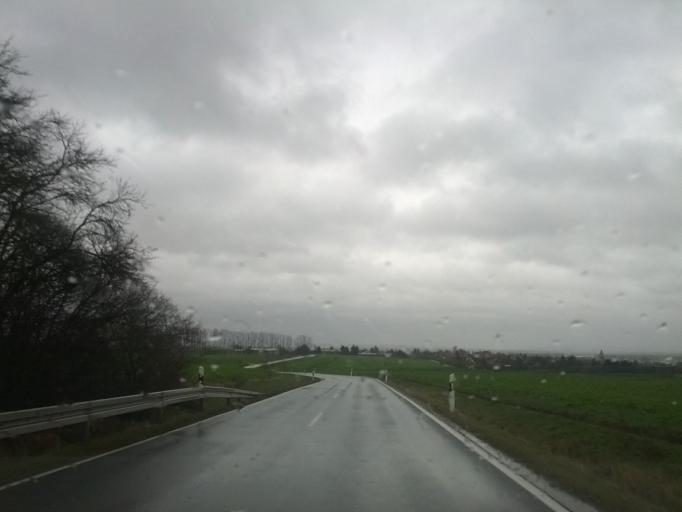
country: DE
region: Thuringia
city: Oberdorla
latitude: 51.1698
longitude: 10.4029
